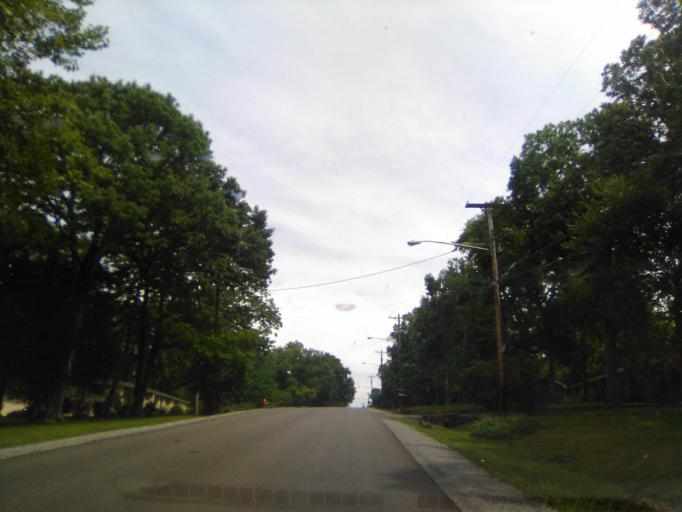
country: US
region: Tennessee
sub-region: Davidson County
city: Belle Meade
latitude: 36.1214
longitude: -86.8952
